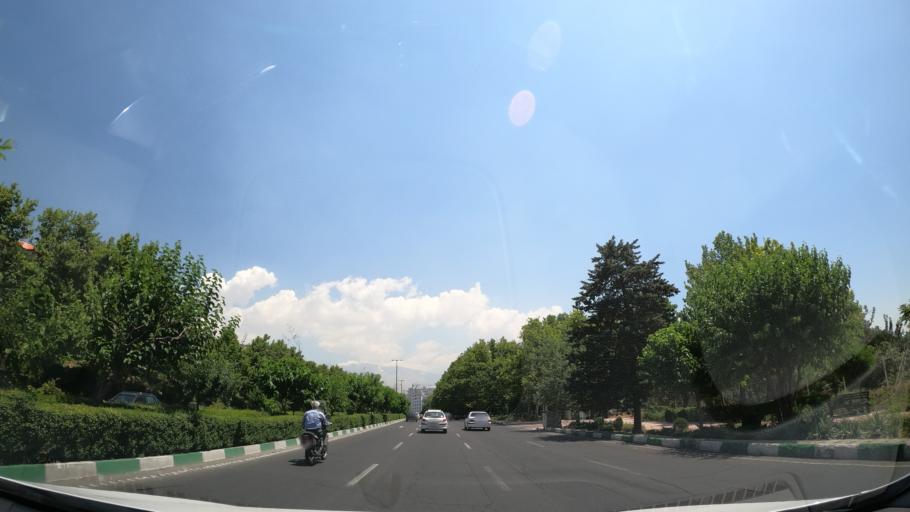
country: IR
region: Tehran
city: Tajrish
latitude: 35.7638
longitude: 51.3770
